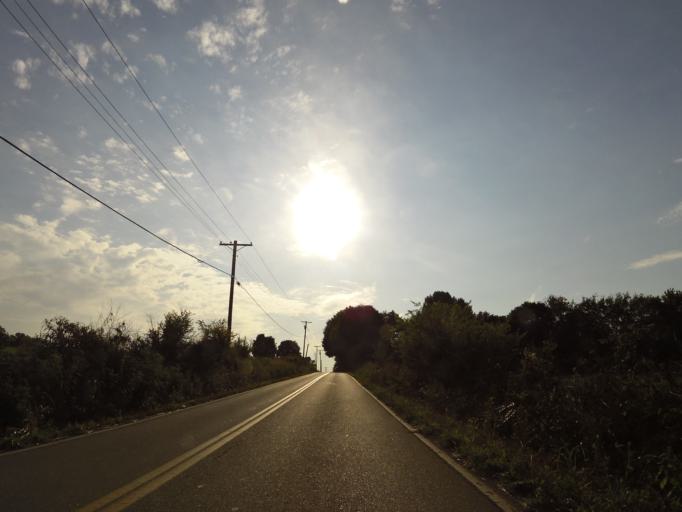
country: US
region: Tennessee
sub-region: Monroe County
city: Madisonville
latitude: 35.6000
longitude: -84.3698
